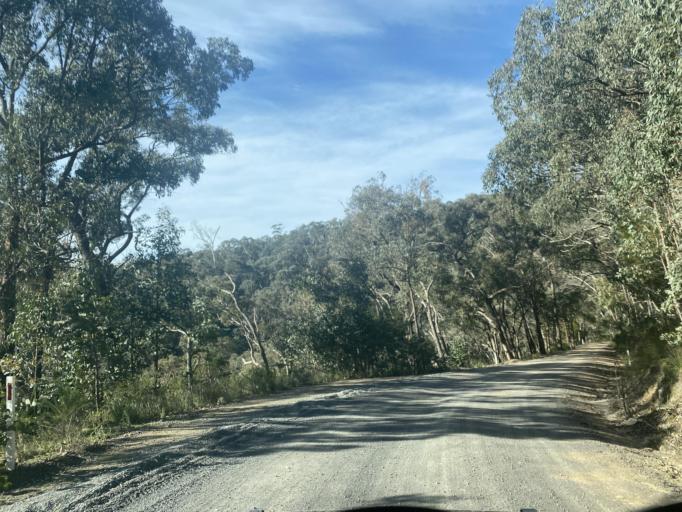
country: AU
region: Victoria
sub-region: Mansfield
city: Mansfield
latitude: -36.8440
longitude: 146.1658
